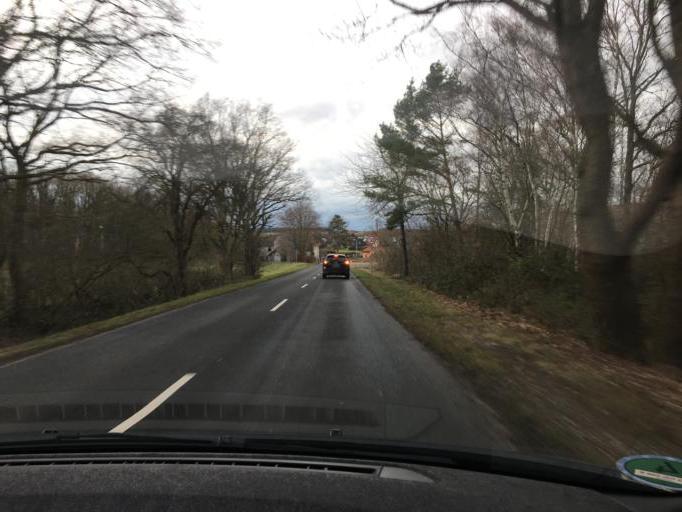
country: DE
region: North Rhine-Westphalia
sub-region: Regierungsbezirk Koln
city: Mechernich
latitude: 50.6250
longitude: 6.6961
